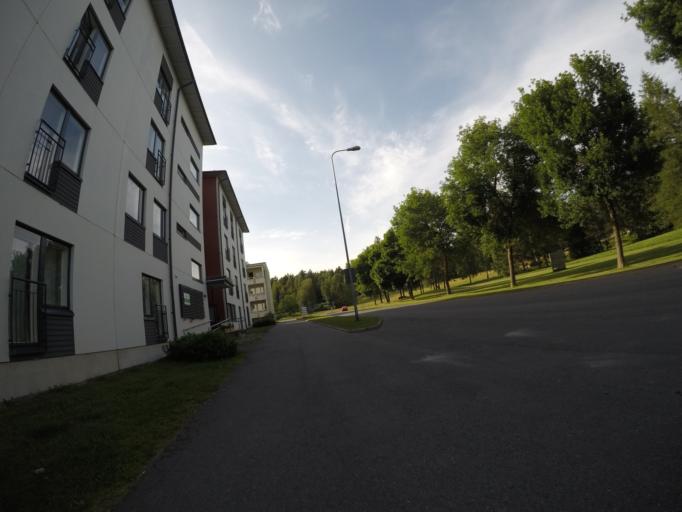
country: FI
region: Haeme
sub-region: Haemeenlinna
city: Haemeenlinna
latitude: 60.9859
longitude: 24.4206
